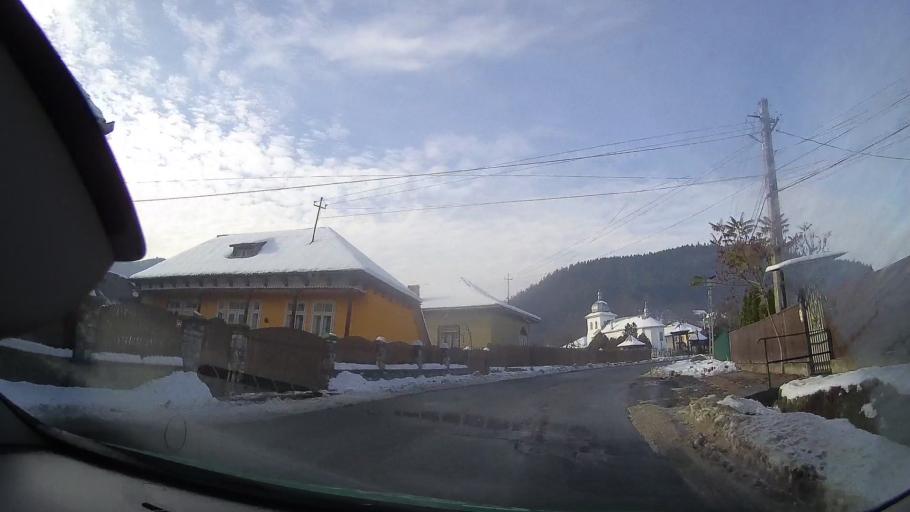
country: RO
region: Neamt
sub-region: Comuna Garcina
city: Garcina
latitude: 46.9770
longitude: 26.3453
